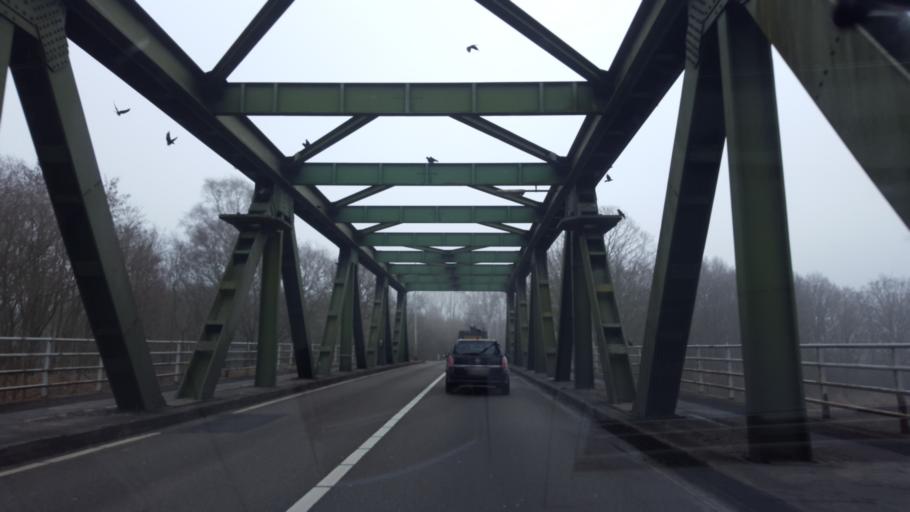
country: NL
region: Limburg
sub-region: Gemeente Leudal
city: Kelpen-Oler
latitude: 51.2353
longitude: 5.7970
